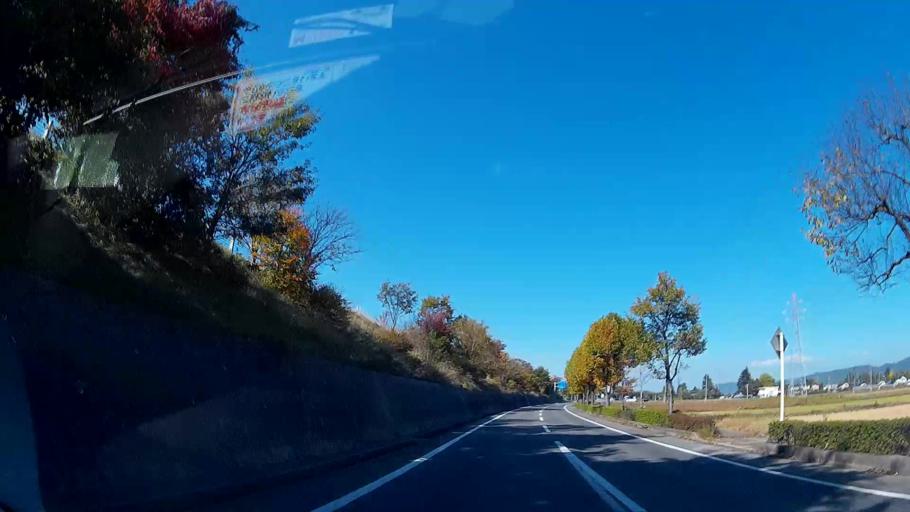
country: JP
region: Nagano
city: Matsumoto
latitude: 36.2061
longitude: 137.9307
